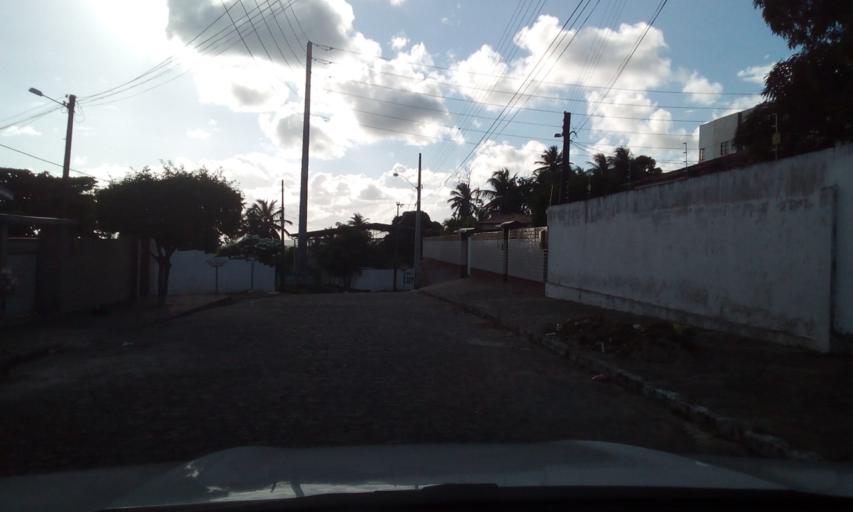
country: BR
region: Paraiba
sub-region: Joao Pessoa
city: Joao Pessoa
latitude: -7.1091
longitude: -34.8694
